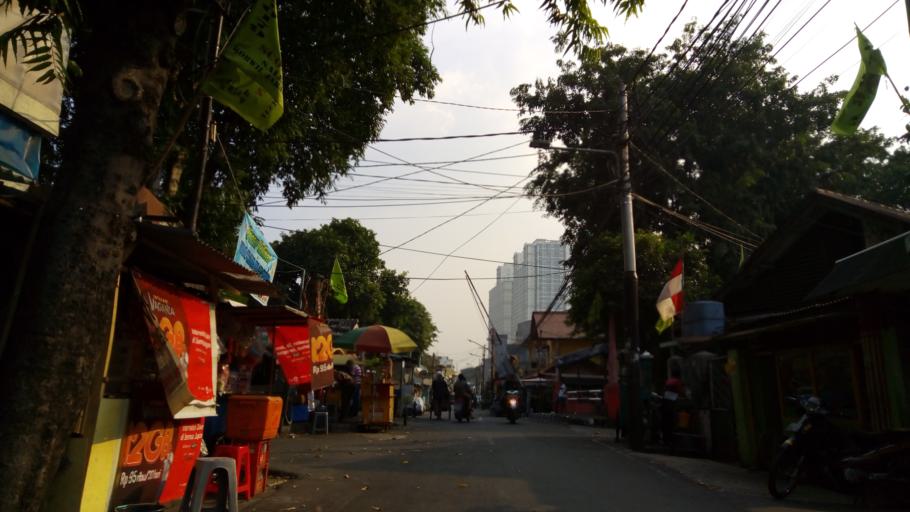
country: ID
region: Jakarta Raya
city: Jakarta
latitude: -6.1949
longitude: 106.8545
